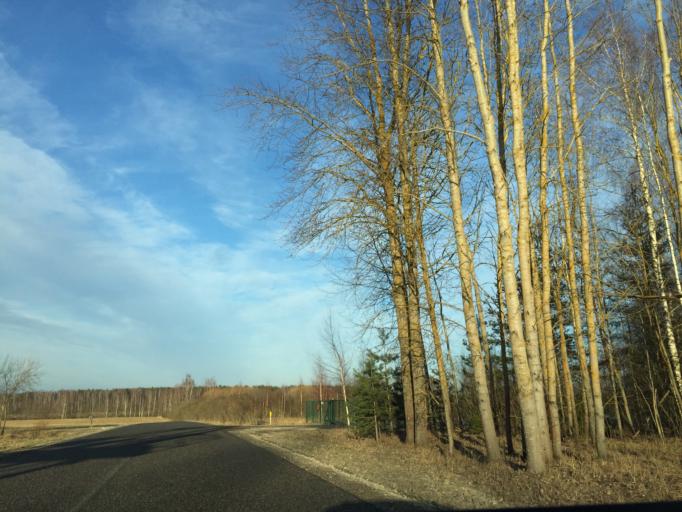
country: LV
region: Kekava
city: Kekava
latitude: 56.8126
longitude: 24.1825
